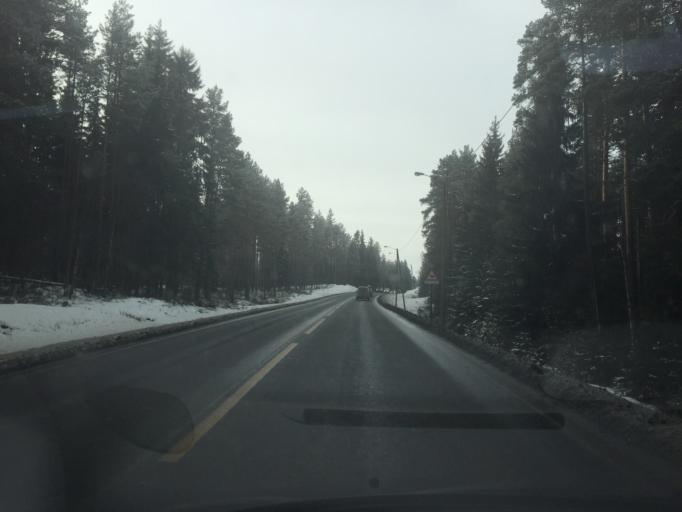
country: NO
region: Hedmark
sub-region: Elverum
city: Elverum
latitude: 60.8823
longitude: 11.5078
